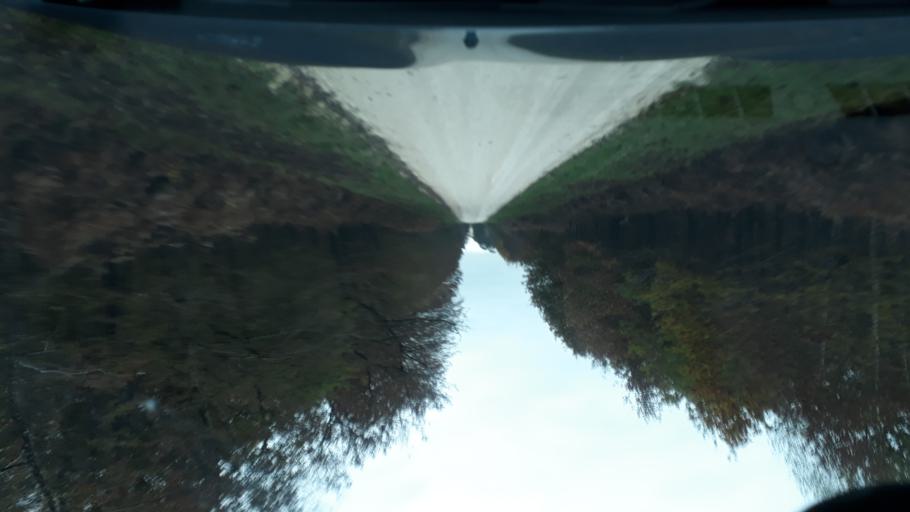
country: FR
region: Centre
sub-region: Departement du Loiret
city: Ouzouer-sur-Loire
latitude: 47.8297
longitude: 2.4737
